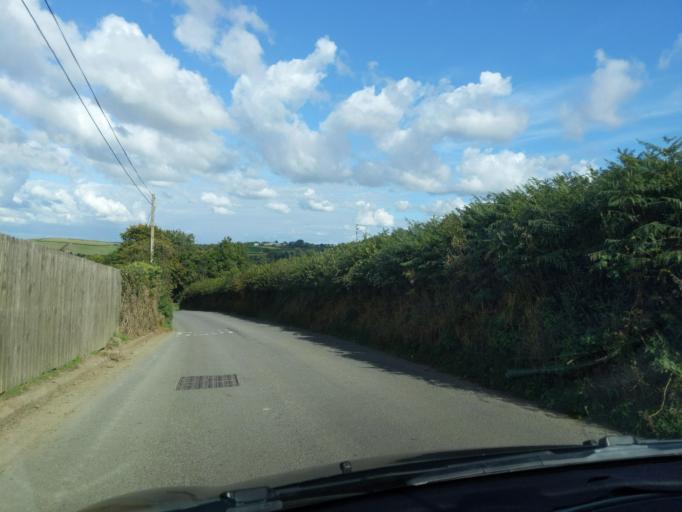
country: GB
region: England
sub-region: Devon
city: Great Torrington
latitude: 50.9302
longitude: -4.1918
